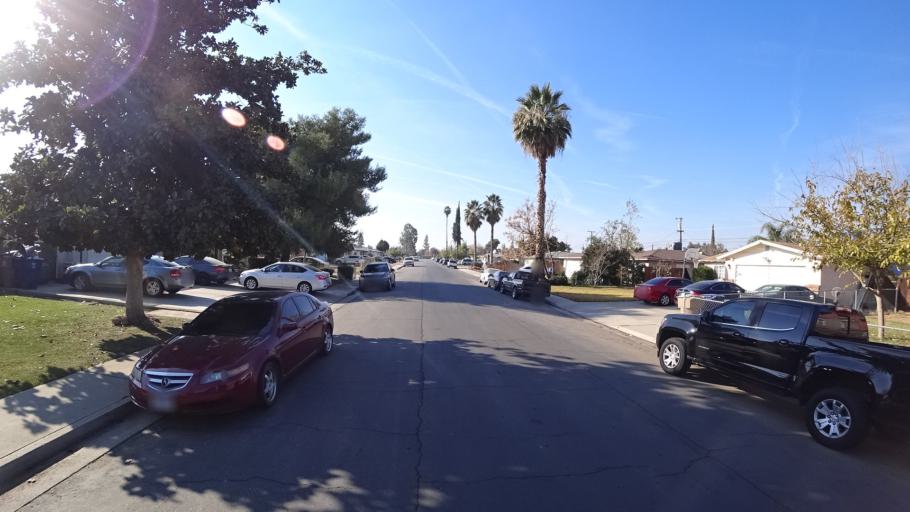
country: US
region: California
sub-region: Kern County
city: Bakersfield
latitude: 35.3208
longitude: -119.0166
